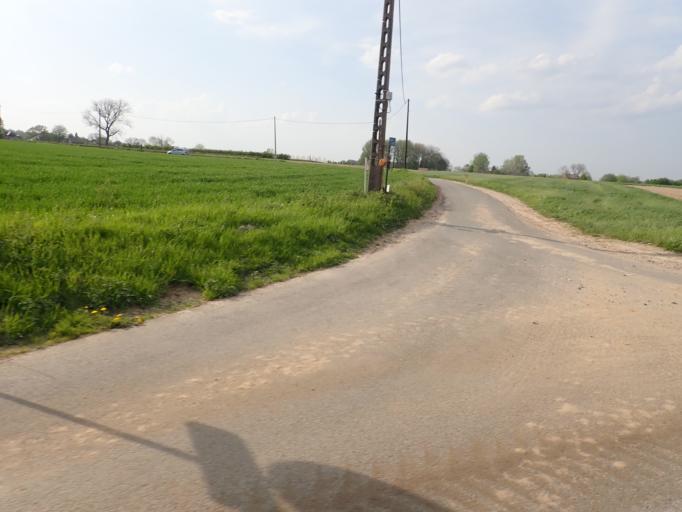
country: BE
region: Flanders
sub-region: Provincie Vlaams-Brabant
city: Wemmel
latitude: 50.9408
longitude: 4.2767
